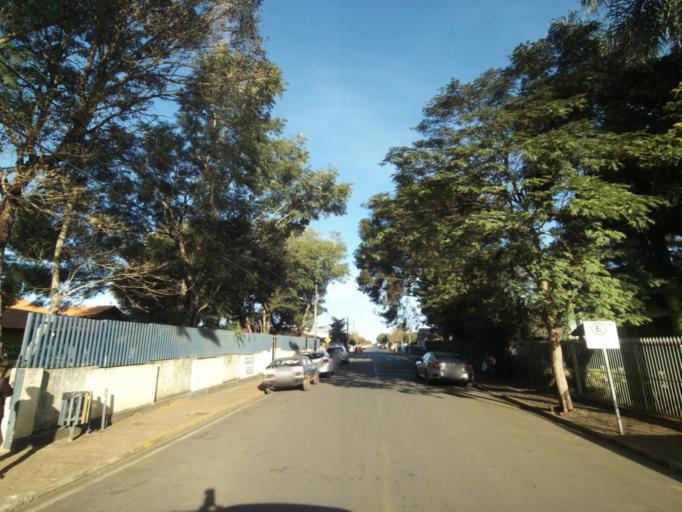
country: BR
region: Parana
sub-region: Tibagi
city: Tibagi
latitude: -24.5110
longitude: -50.4127
